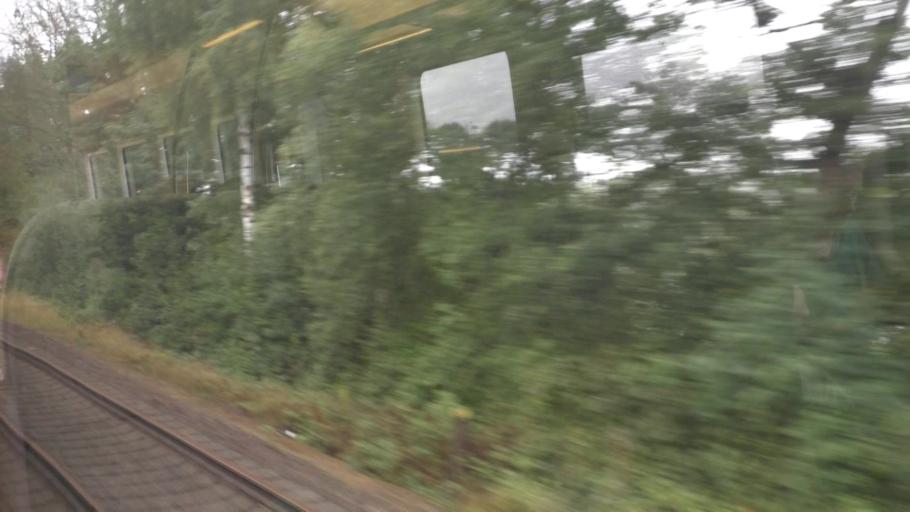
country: DE
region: Saxony
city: Radeberg
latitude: 51.1073
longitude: 13.9274
